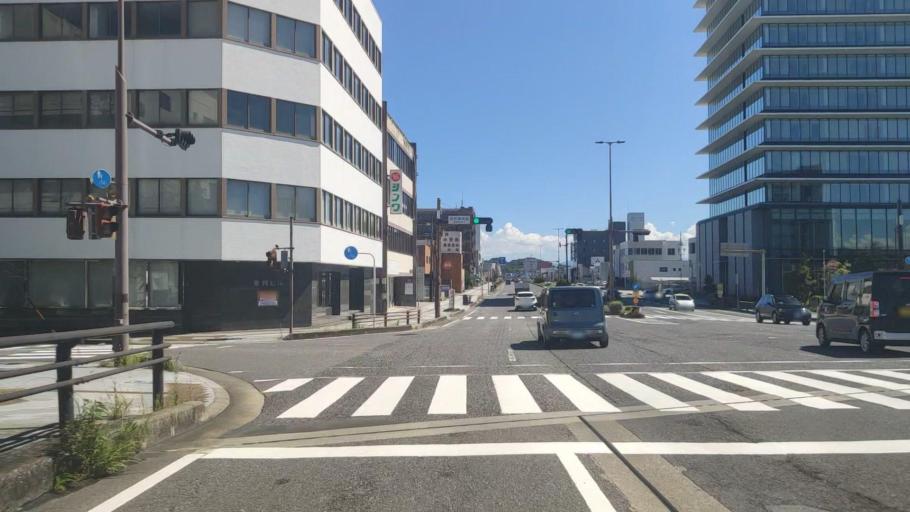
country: JP
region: Mie
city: Tsu-shi
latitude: 34.7135
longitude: 136.5091
